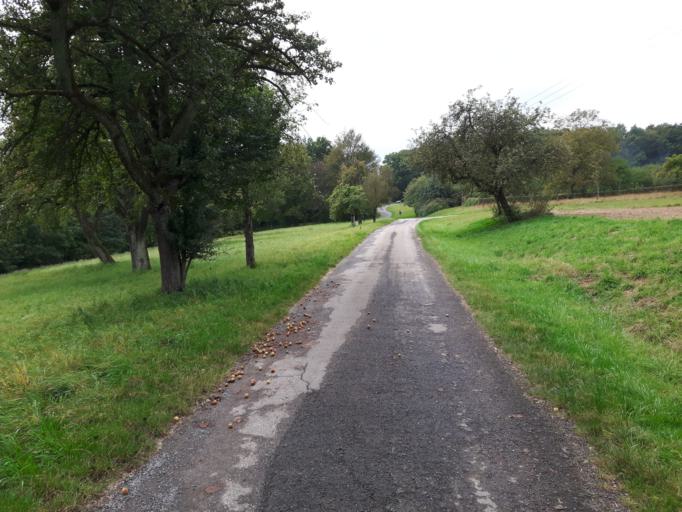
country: DE
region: Baden-Wuerttemberg
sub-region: Karlsruhe Region
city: Maulbronn
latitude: 49.0043
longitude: 8.8148
